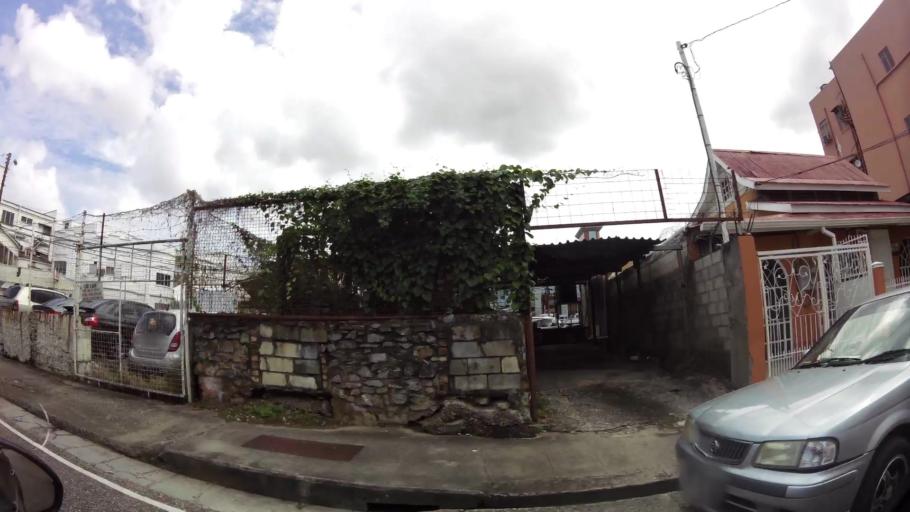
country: TT
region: City of Port of Spain
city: Port-of-Spain
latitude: 10.6570
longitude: -61.5130
